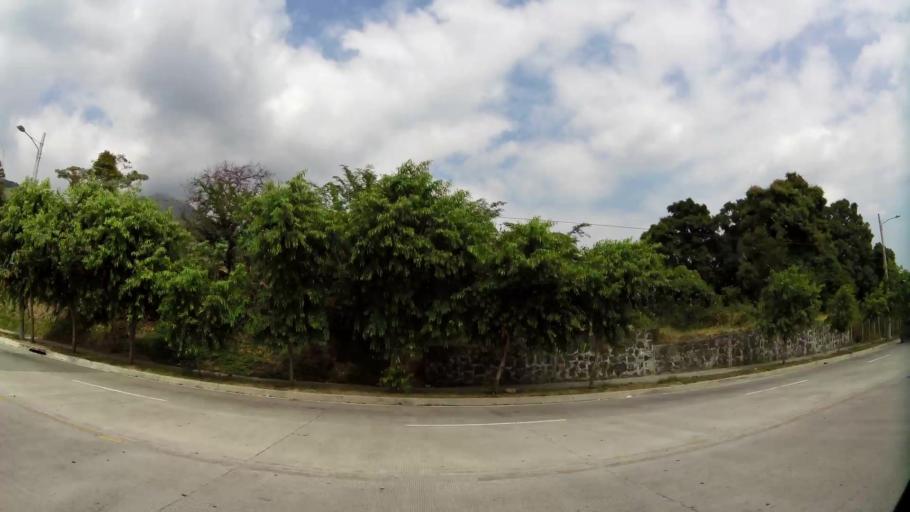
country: SV
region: San Salvador
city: Mejicanos
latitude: 13.7141
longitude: -89.2465
